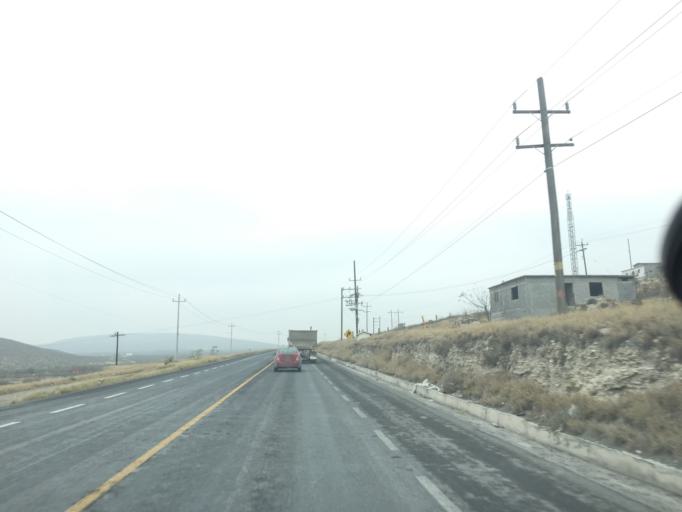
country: MX
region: Nuevo Leon
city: Mina
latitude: 26.0050
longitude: -100.5436
